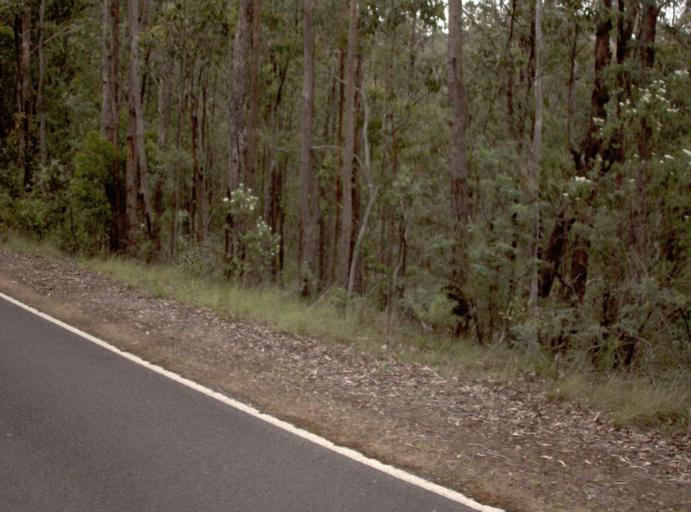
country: AU
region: Victoria
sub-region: East Gippsland
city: Bairnsdale
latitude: -37.6410
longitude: 147.2665
